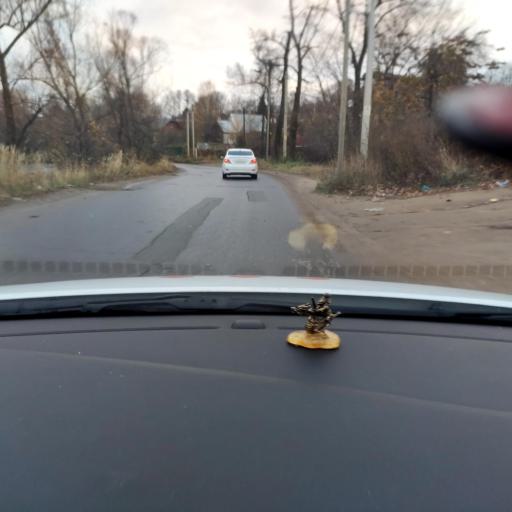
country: RU
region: Tatarstan
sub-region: Gorod Kazan'
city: Kazan
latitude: 55.7258
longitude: 49.1575
